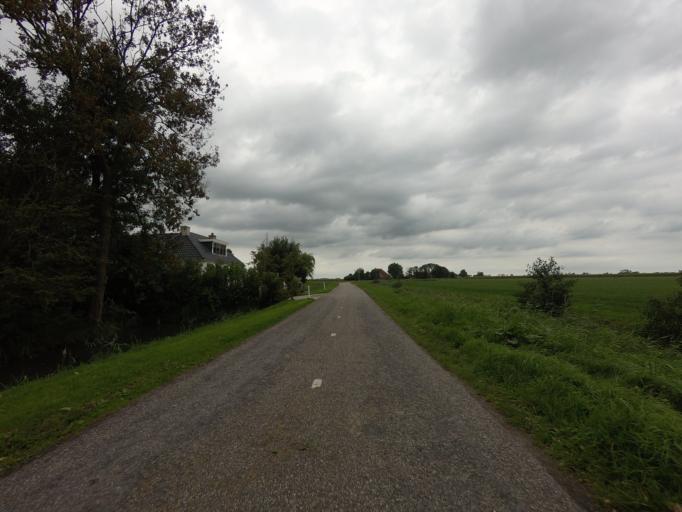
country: NL
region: Friesland
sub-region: Sudwest Fryslan
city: IJlst
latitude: 53.0533
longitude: 5.5974
